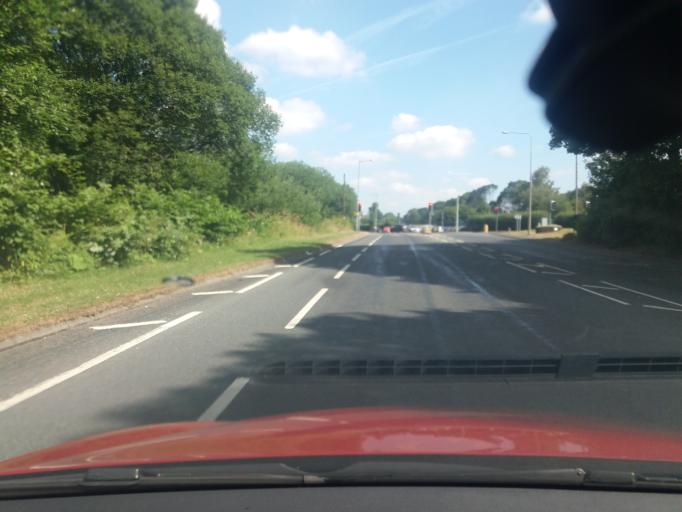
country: GB
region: England
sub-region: Lancashire
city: Adlington
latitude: 53.6279
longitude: -2.6101
